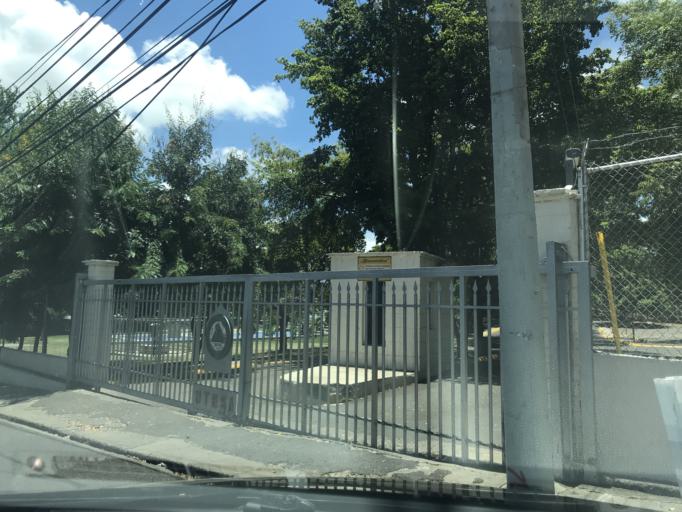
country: DO
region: Santiago
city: Santiago de los Caballeros
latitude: 19.4361
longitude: -70.6948
